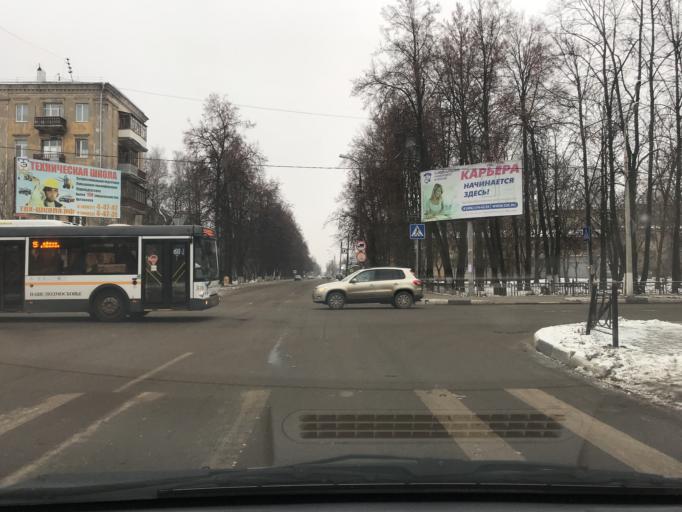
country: RU
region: Moskovskaya
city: Elektrostal'
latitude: 55.7917
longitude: 38.4464
